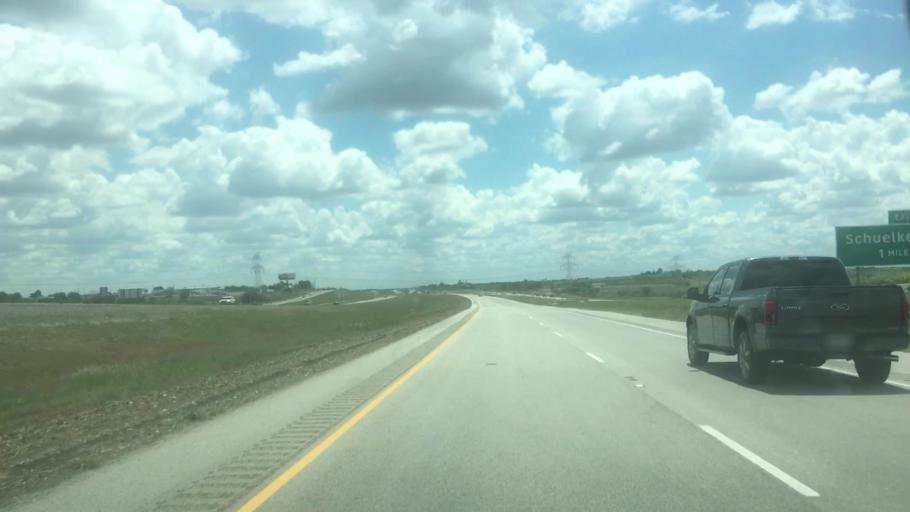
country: US
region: Texas
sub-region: Caldwell County
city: Uhland
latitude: 30.0018
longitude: -97.6870
